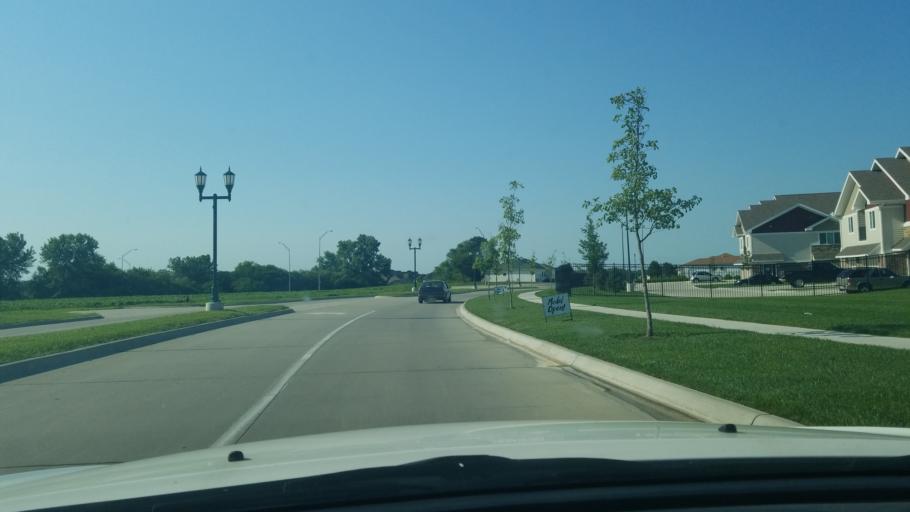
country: US
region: Nebraska
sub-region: Lancaster County
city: Lincoln
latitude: 40.7395
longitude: -96.6011
